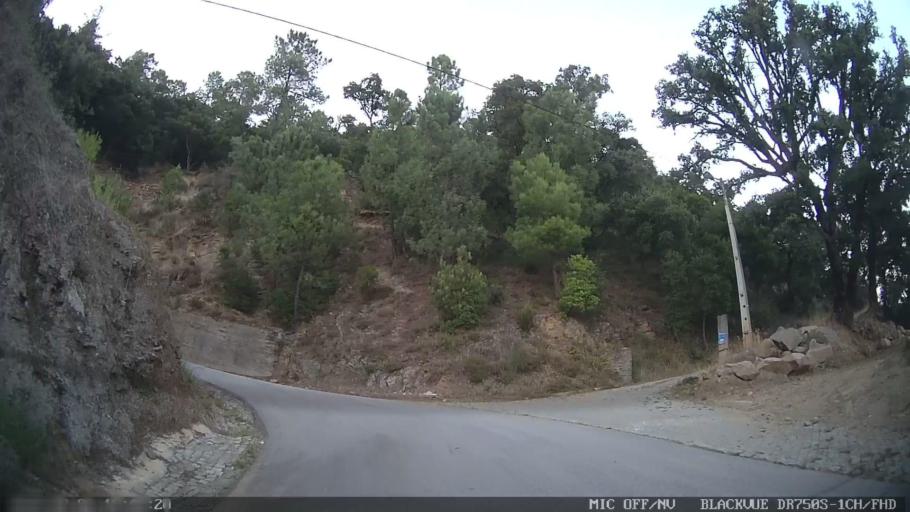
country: PT
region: Vila Real
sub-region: Mesao Frio
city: Mesao Frio
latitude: 41.1633
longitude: -7.8758
